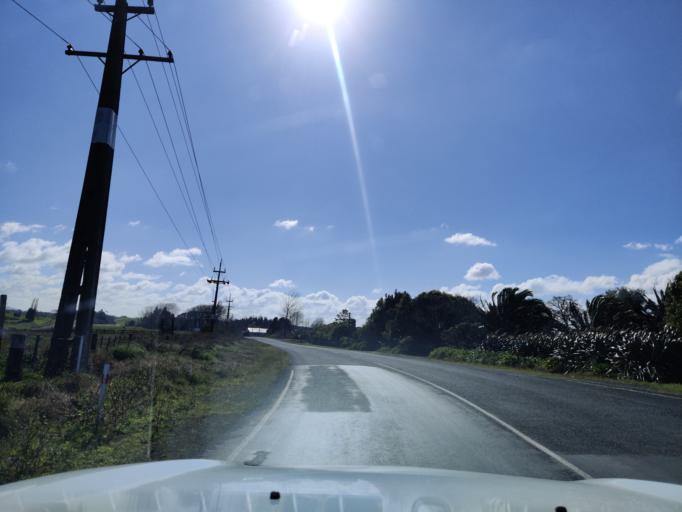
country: NZ
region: Waikato
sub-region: Waikato District
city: Te Kauwhata
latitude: -37.4040
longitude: 175.1227
